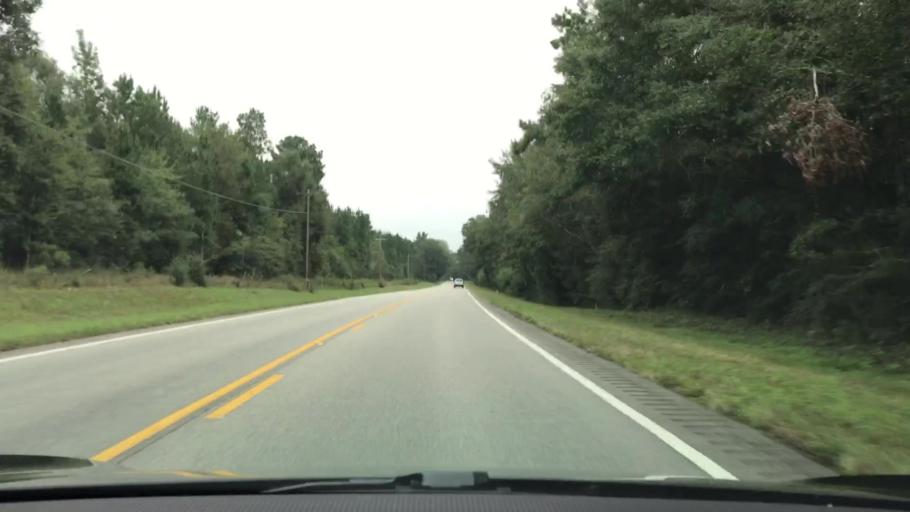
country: US
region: Alabama
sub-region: Coffee County
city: Elba
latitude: 31.4675
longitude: -86.0649
